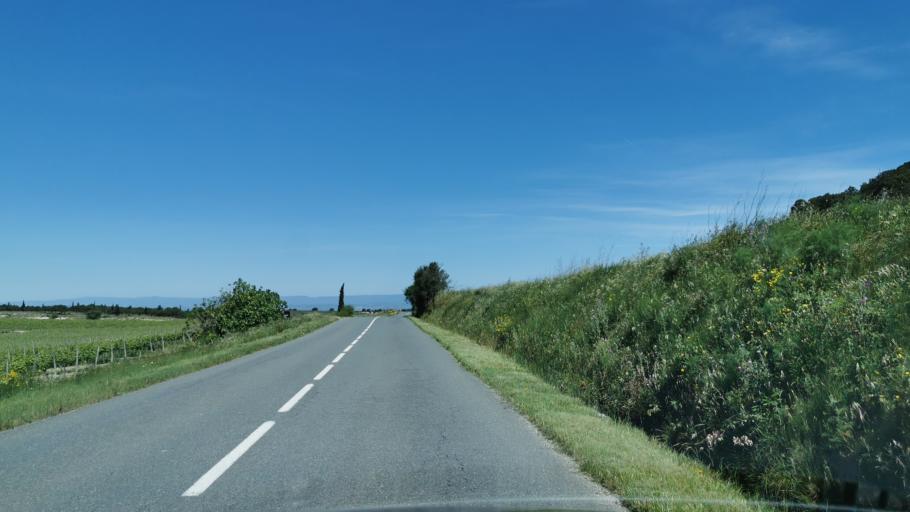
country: FR
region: Languedoc-Roussillon
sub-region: Departement de l'Aude
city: Armissan
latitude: 43.1703
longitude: 3.1145
